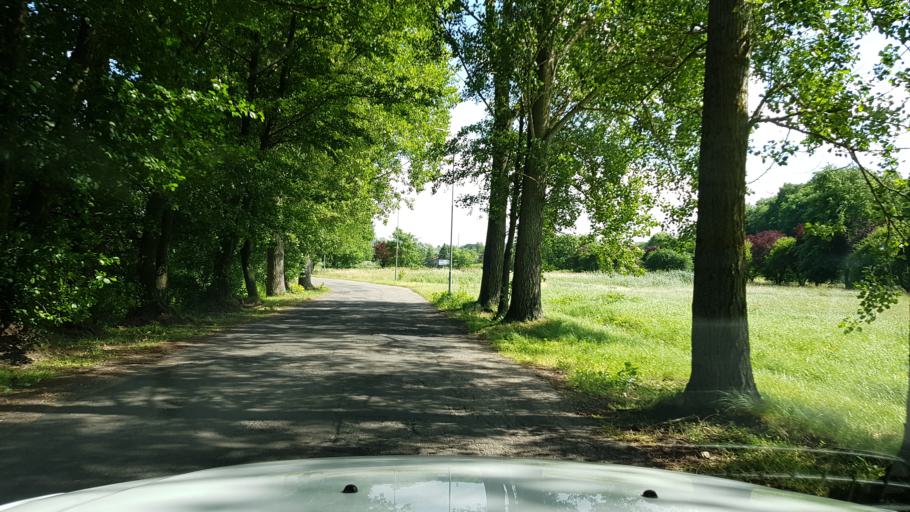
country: PL
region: West Pomeranian Voivodeship
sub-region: Powiat kamienski
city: Kamien Pomorski
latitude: 53.9717
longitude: 14.7790
